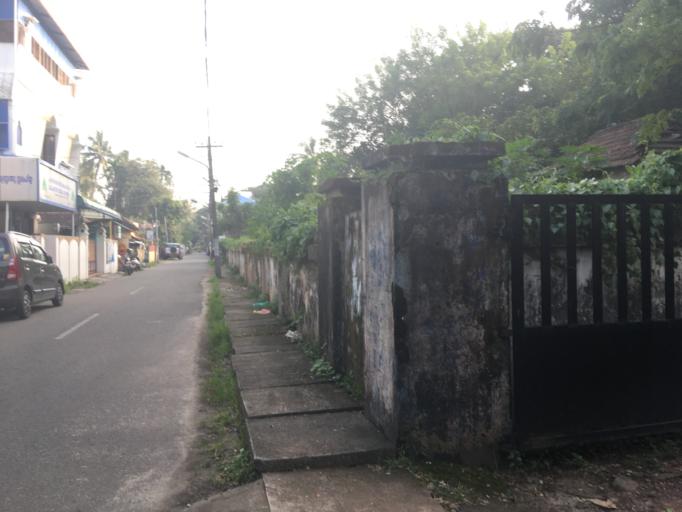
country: IN
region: Kerala
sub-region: Ernakulam
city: Cochin
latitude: 9.9571
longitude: 76.2405
